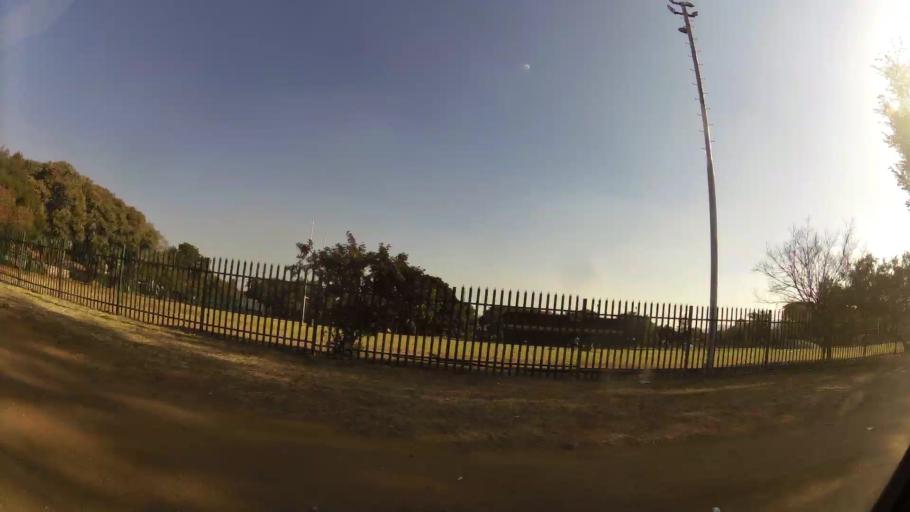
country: ZA
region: North-West
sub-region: Bojanala Platinum District Municipality
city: Rustenburg
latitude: -25.6572
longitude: 27.2579
